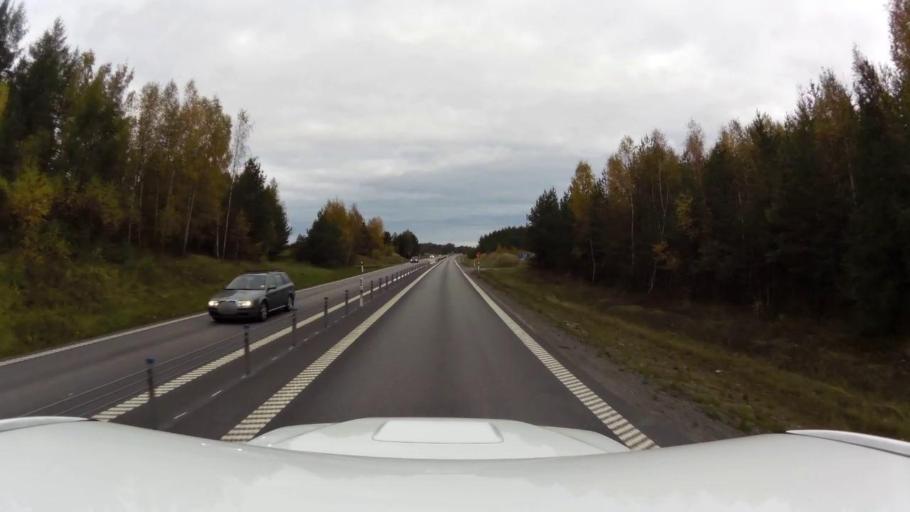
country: SE
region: OEstergoetland
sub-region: Linkopings Kommun
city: Ljungsbro
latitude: 58.4937
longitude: 15.4648
